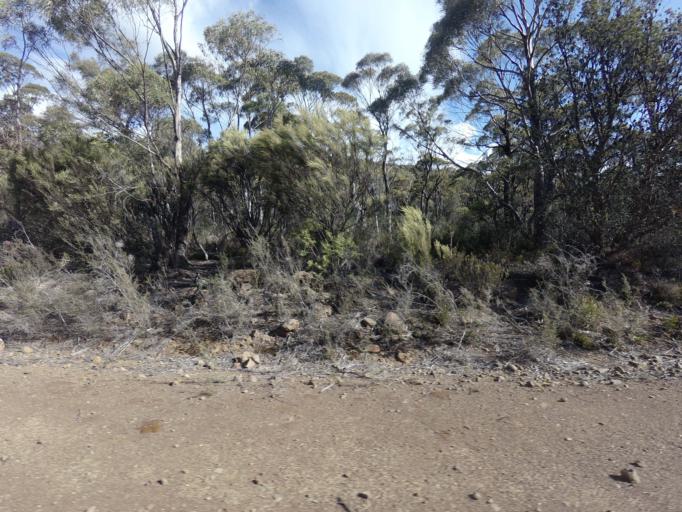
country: AU
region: Tasmania
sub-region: Break O'Day
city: St Helens
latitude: -41.8556
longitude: 148.0308
